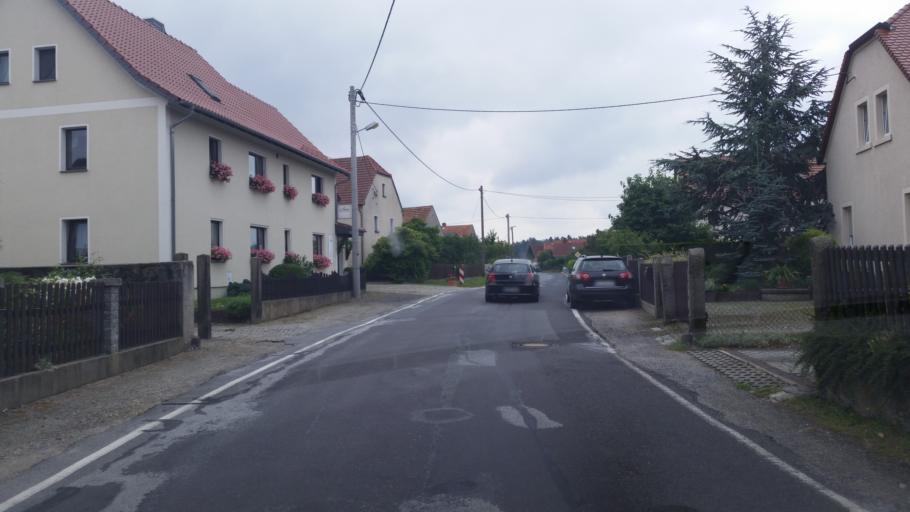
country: DE
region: Saxony
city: Laussnitz
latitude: 51.2451
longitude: 13.8824
